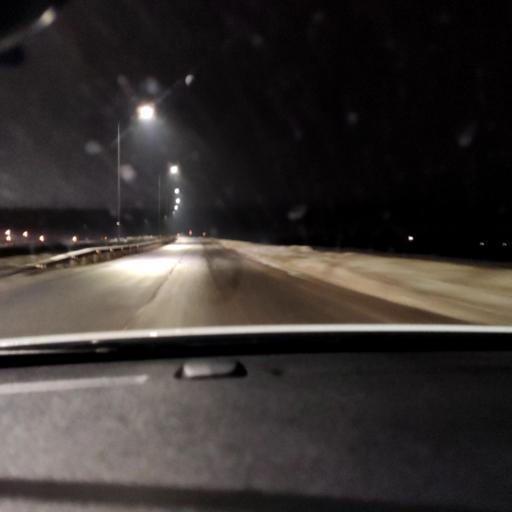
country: RU
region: Tatarstan
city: Sviyazhsk
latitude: 55.7424
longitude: 48.7756
